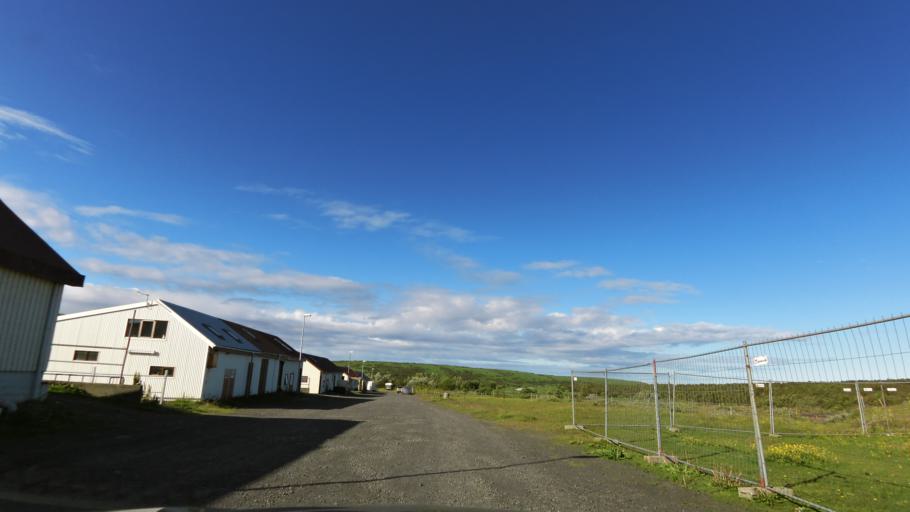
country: IS
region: Capital Region
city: Reykjavik
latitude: 64.0800
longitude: -21.8457
